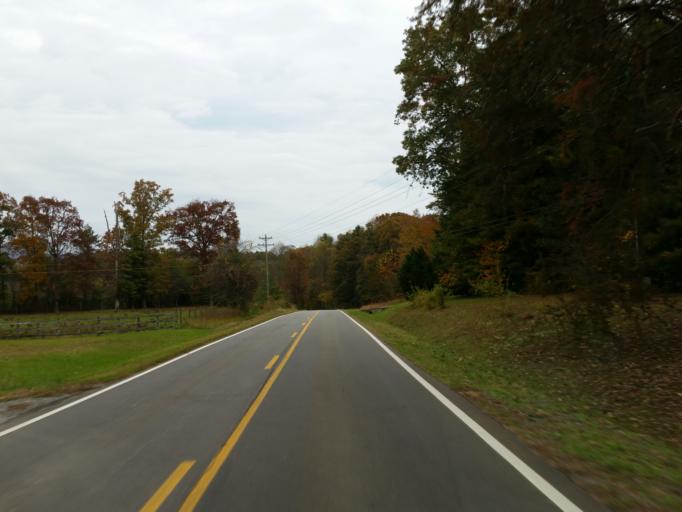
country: US
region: Georgia
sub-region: Gilmer County
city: Ellijay
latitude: 34.6534
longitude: -84.3826
